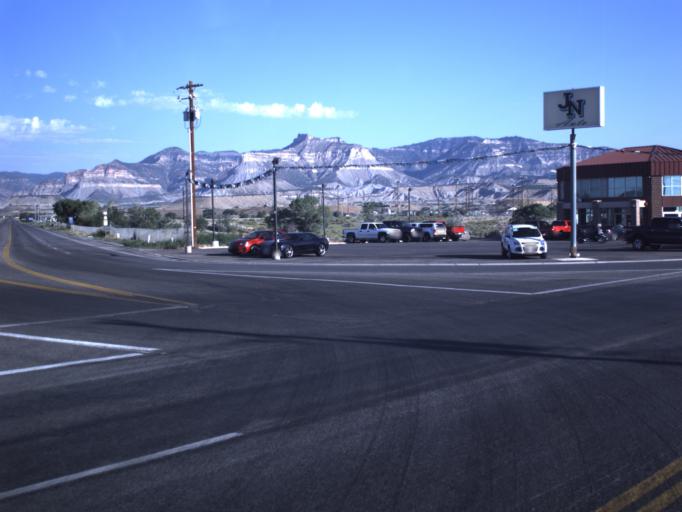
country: US
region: Utah
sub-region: Emery County
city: Huntington
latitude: 39.3343
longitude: -110.9647
